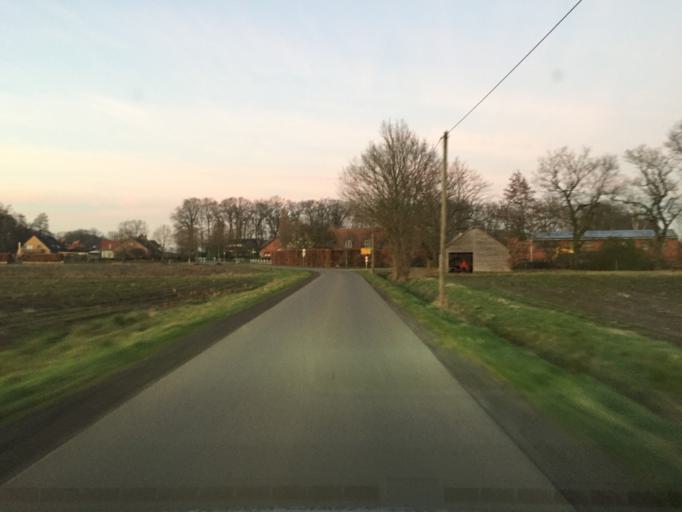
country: DE
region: Lower Saxony
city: Hassel
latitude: 52.6636
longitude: 8.8373
